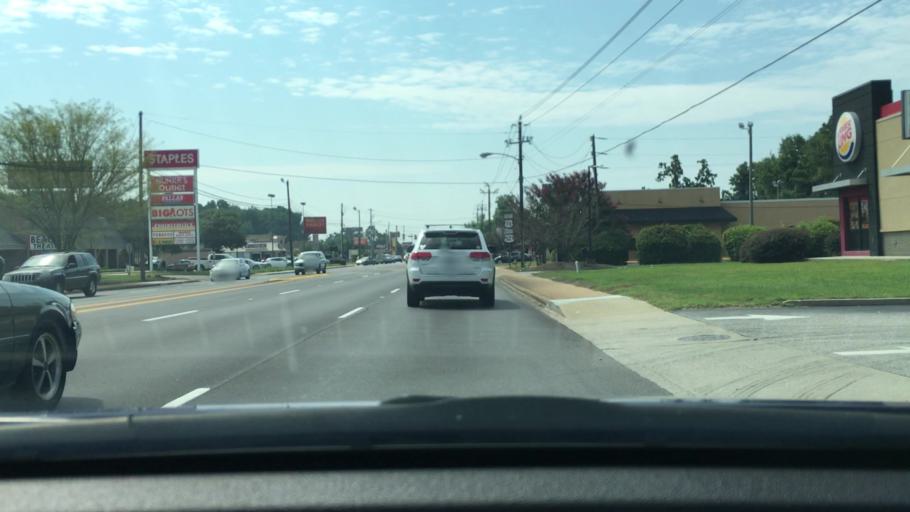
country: US
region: South Carolina
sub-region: Sumter County
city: Sumter
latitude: 33.9538
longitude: -80.3790
